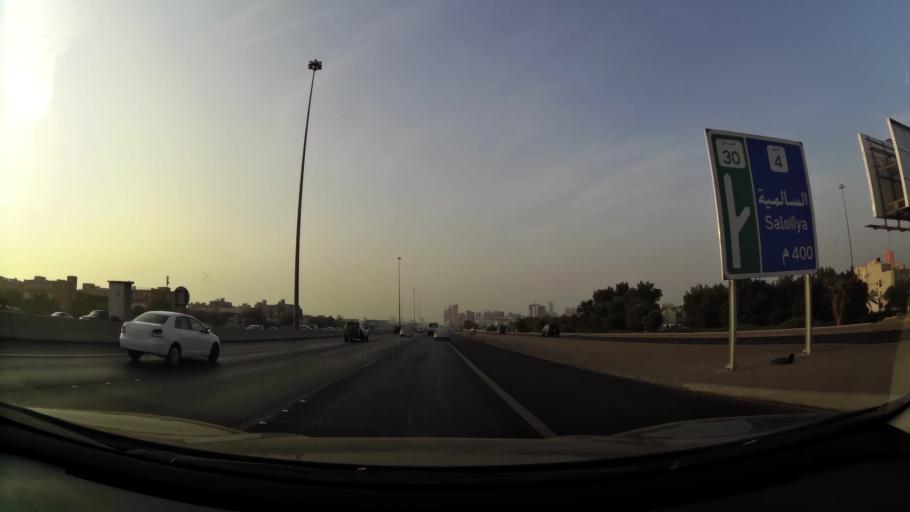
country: KW
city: Bayan
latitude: 29.3156
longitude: 48.0521
